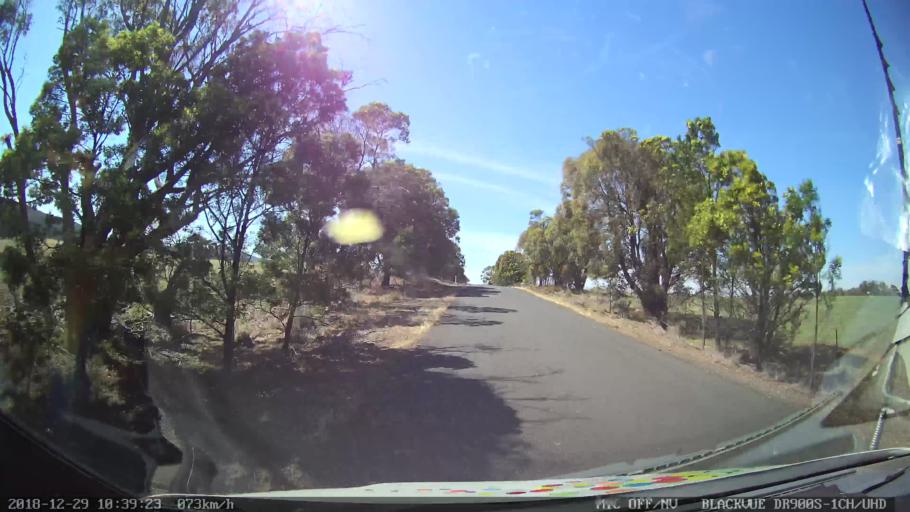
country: AU
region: New South Wales
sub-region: Palerang
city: Bungendore
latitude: -35.0060
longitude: 149.5101
